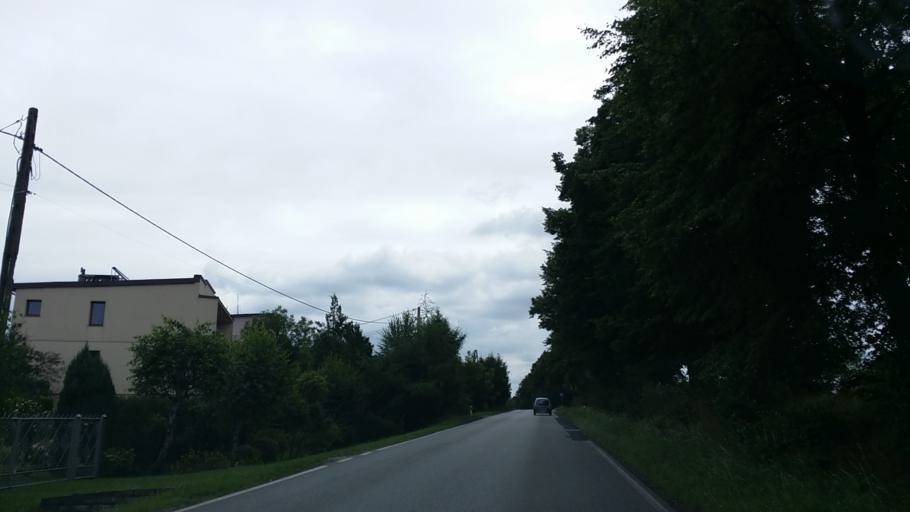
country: PL
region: Lesser Poland Voivodeship
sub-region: Powiat wadowicki
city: Chocznia
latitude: 49.8929
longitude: 19.4602
